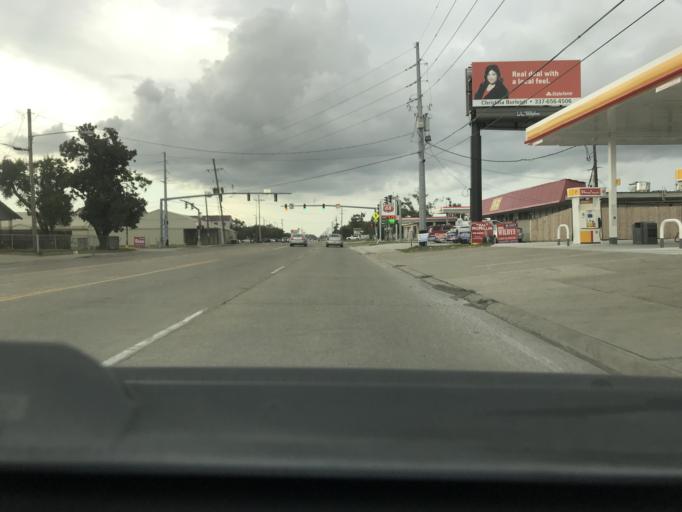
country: US
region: Louisiana
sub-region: Calcasieu Parish
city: Westlake
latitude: 30.2470
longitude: -93.2580
